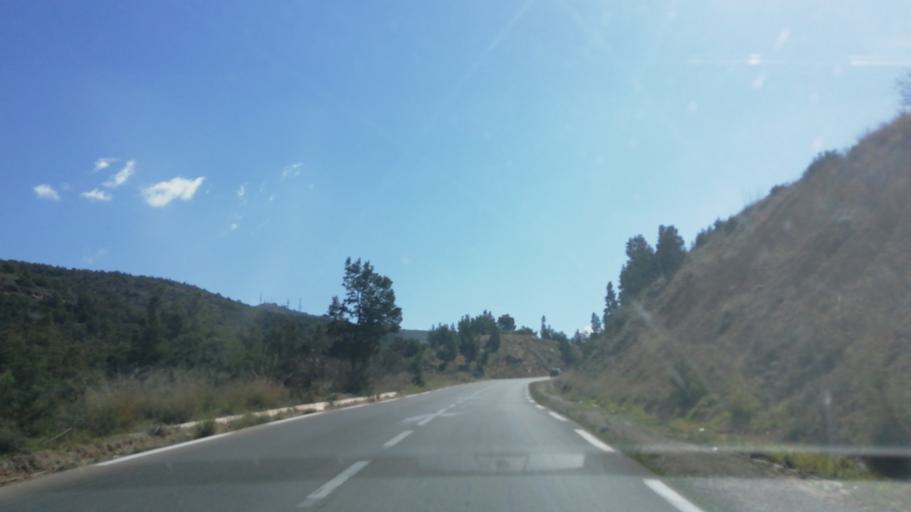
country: DZ
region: Mascara
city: Mascara
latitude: 35.4889
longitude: 0.1447
